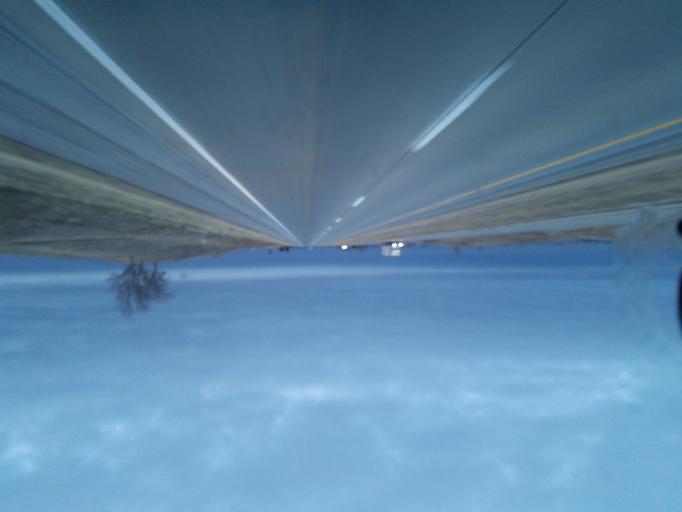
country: US
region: Iowa
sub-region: Pottawattamie County
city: Avoca
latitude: 41.4980
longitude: -95.1639
